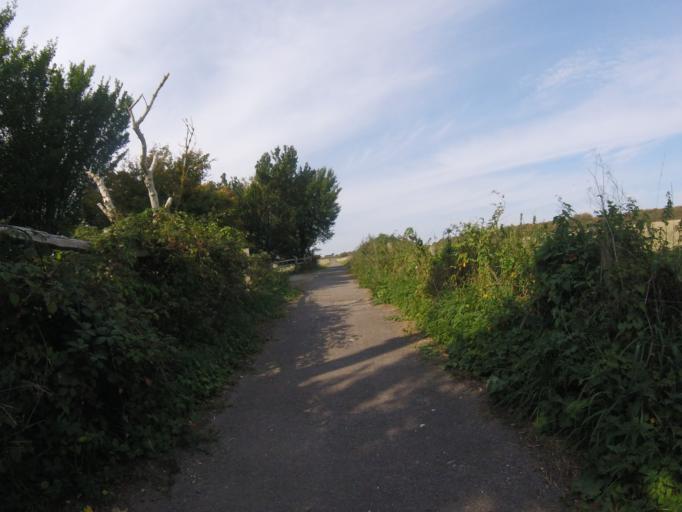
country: GB
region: England
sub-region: West Sussex
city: Fulking
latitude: 50.8728
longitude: -0.2000
